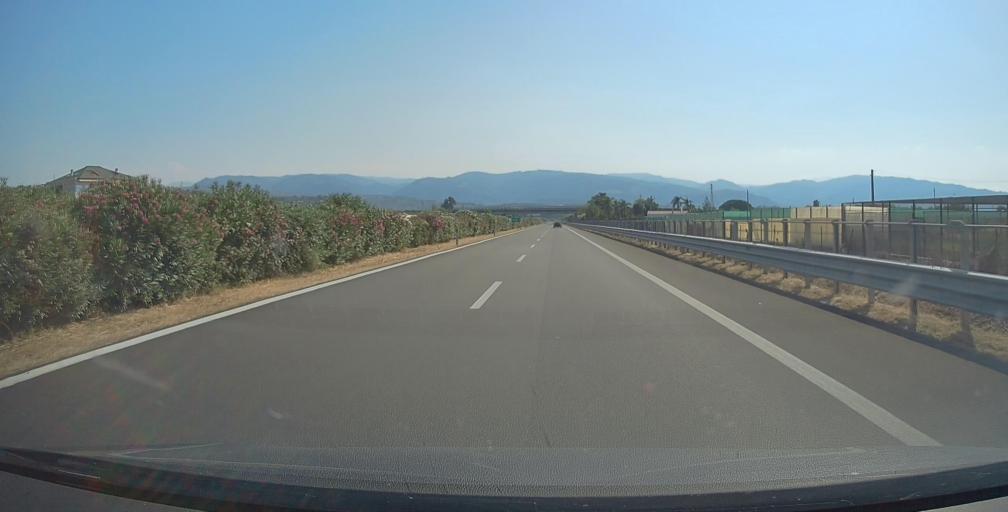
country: IT
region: Sicily
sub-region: Messina
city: Vigliatore 2
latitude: 38.1272
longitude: 15.1269
